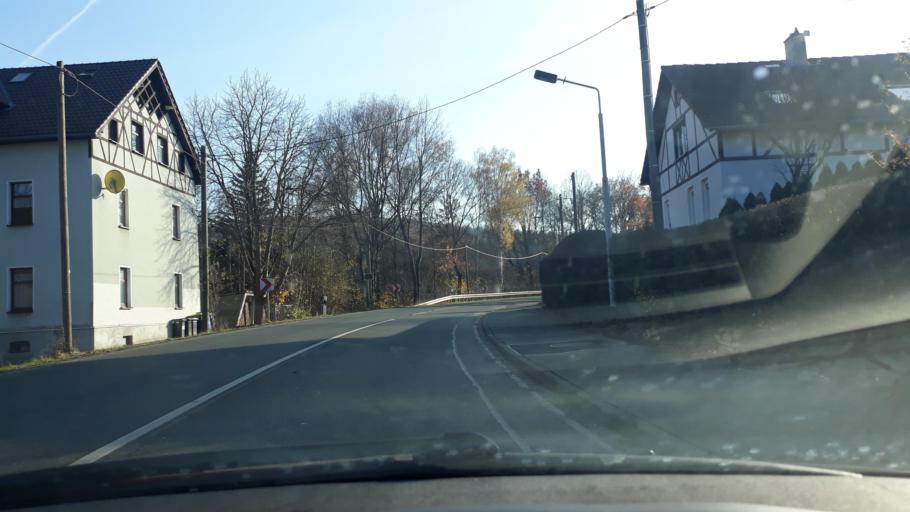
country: DE
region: Saxony
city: Wilkau-Hasslau
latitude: 50.6616
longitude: 12.5240
